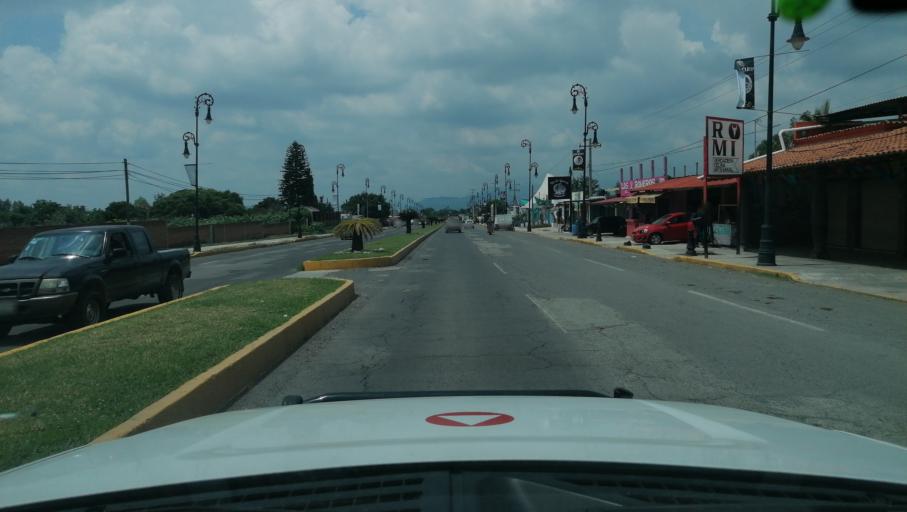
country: MX
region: Morelos
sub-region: Yecapixtla
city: Yecapixtla
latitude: 18.8855
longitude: -98.8710
